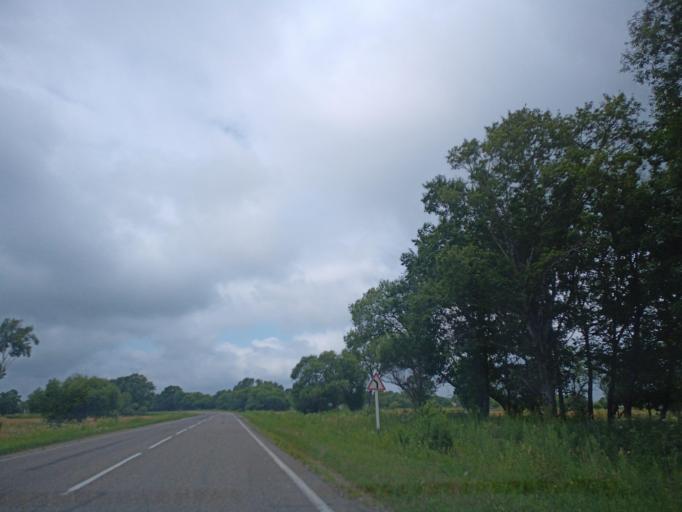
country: RU
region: Primorskiy
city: Dal'nerechensk
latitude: 45.9465
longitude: 133.8893
